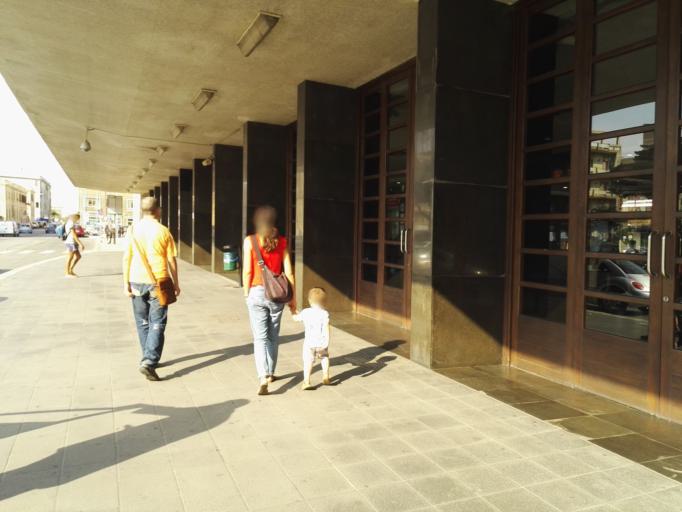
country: IT
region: Calabria
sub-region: Provincia di Reggio Calabria
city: Reggio Calabria
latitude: 38.1035
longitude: 15.6366
